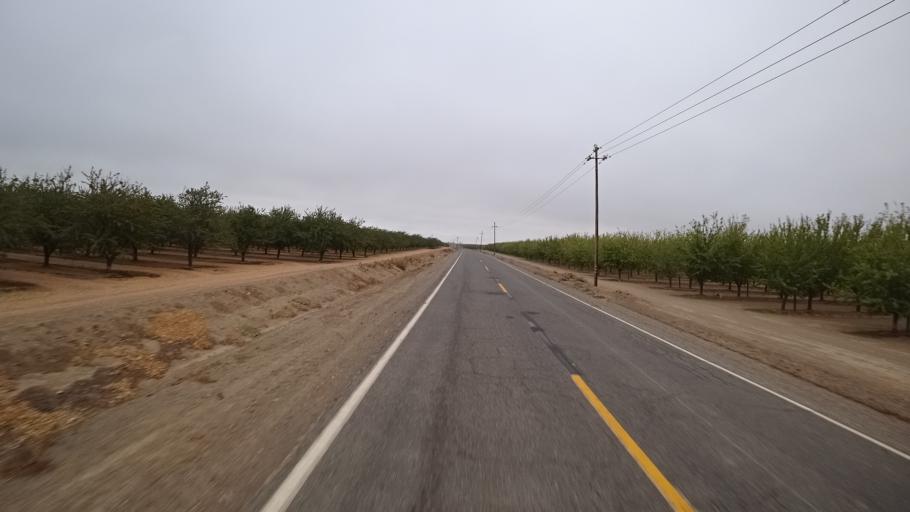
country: US
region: California
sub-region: Yolo County
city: Dunnigan
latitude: 38.9257
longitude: -122.0112
